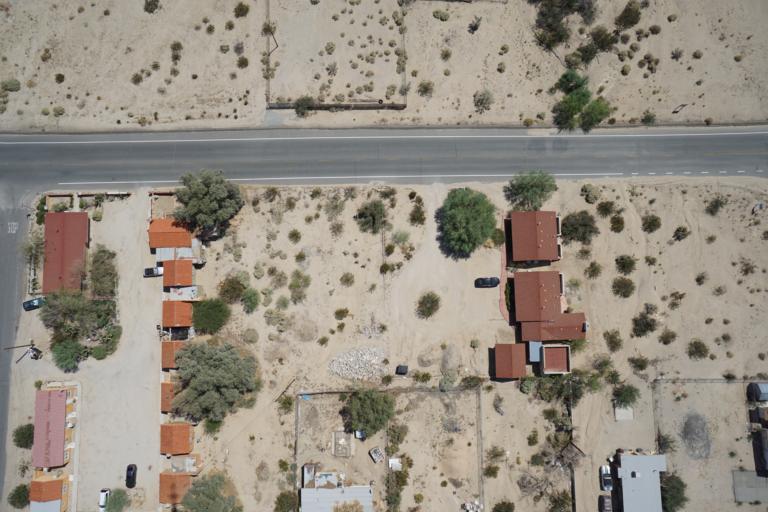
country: US
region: California
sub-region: San Bernardino County
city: Twentynine Palms
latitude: 34.1329
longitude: -116.0547
